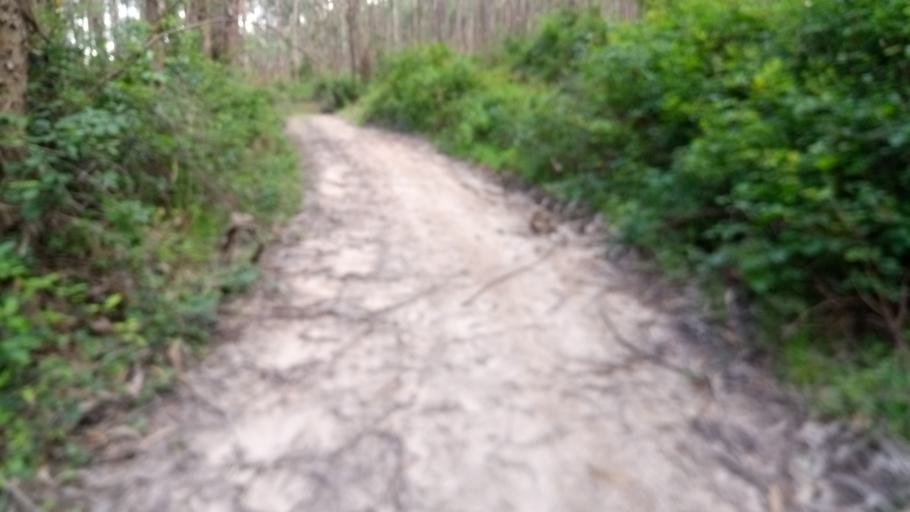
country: PT
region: Leiria
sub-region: Obidos
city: Obidos
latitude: 39.3925
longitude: -9.2081
